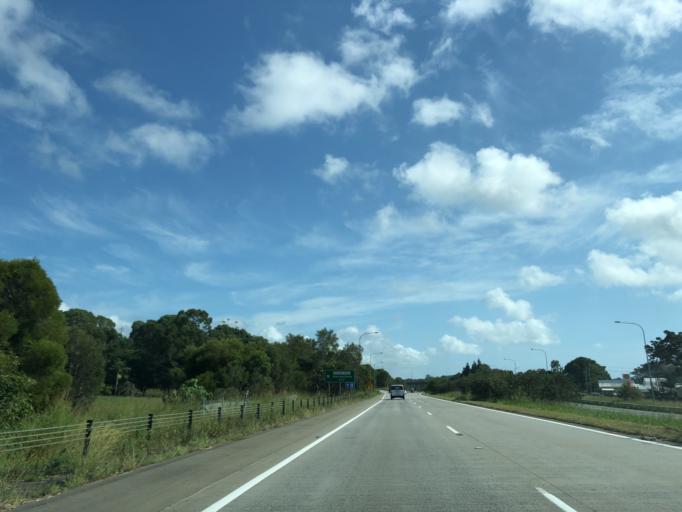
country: AU
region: New South Wales
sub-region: Byron Shire
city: Brunswick Heads
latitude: -28.5888
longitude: 153.5445
